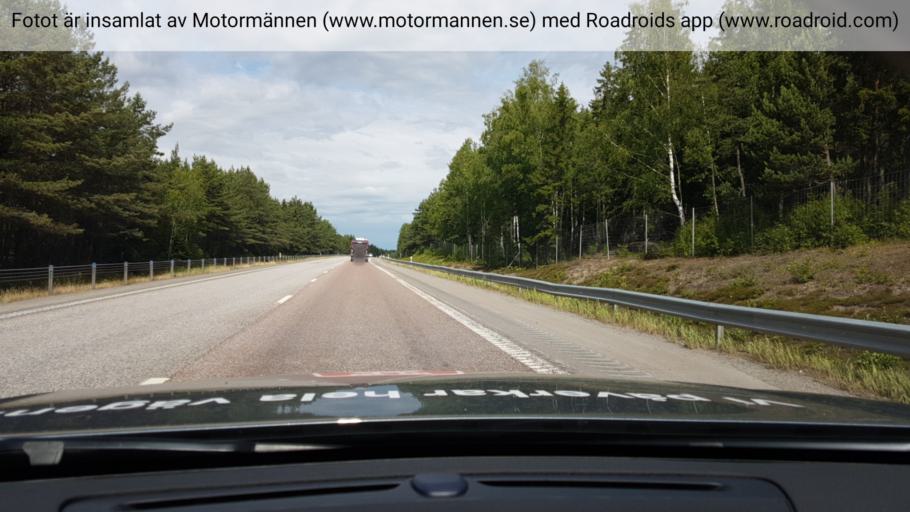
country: SE
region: Uppsala
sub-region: Knivsta Kommun
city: Knivsta
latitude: 59.7502
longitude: 17.8129
